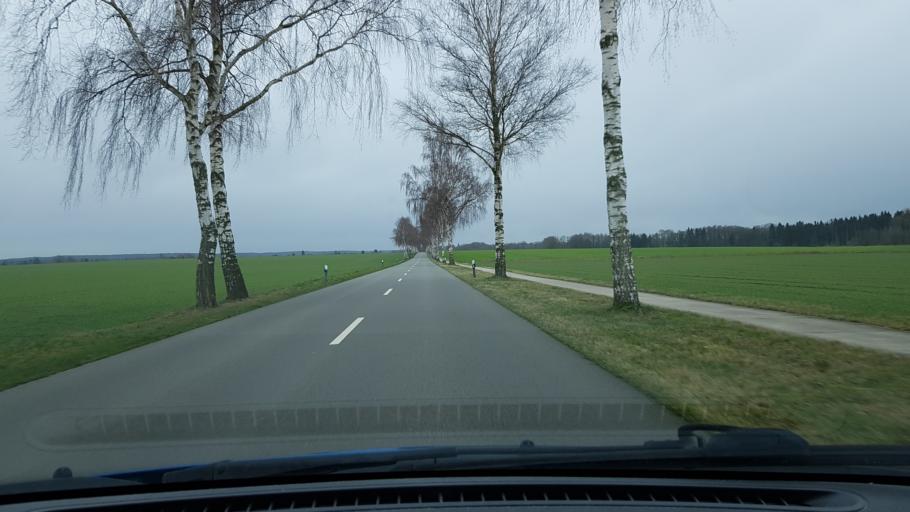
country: DE
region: Lower Saxony
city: Wrestedt
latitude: 52.9203
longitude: 10.5689
